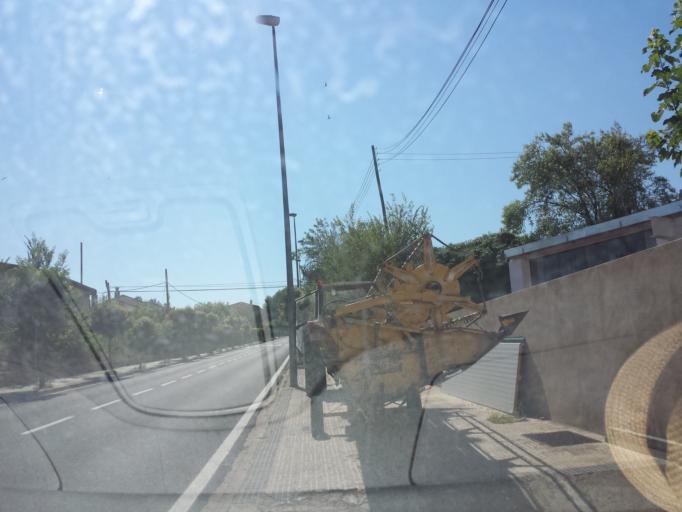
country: ES
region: Aragon
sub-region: Provincia de Zaragoza
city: Nuevalos
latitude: 41.2119
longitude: -1.7892
